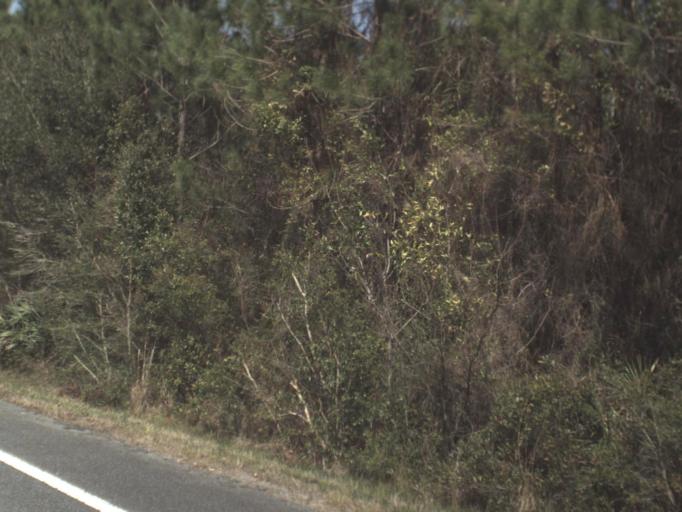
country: US
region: Florida
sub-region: Franklin County
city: Carrabelle
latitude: 29.9718
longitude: -84.4987
